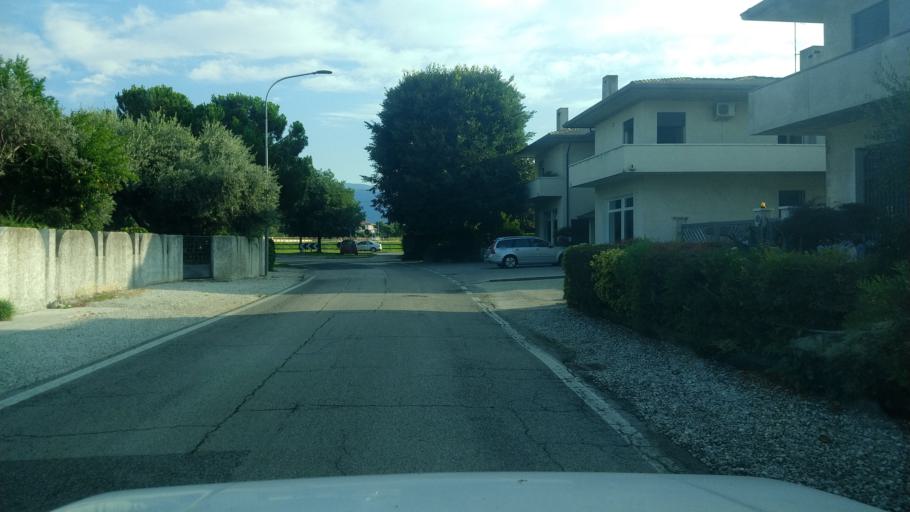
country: IT
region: Veneto
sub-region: Provincia di Vicenza
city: Bassano del Grappa
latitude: 45.7324
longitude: 11.7236
